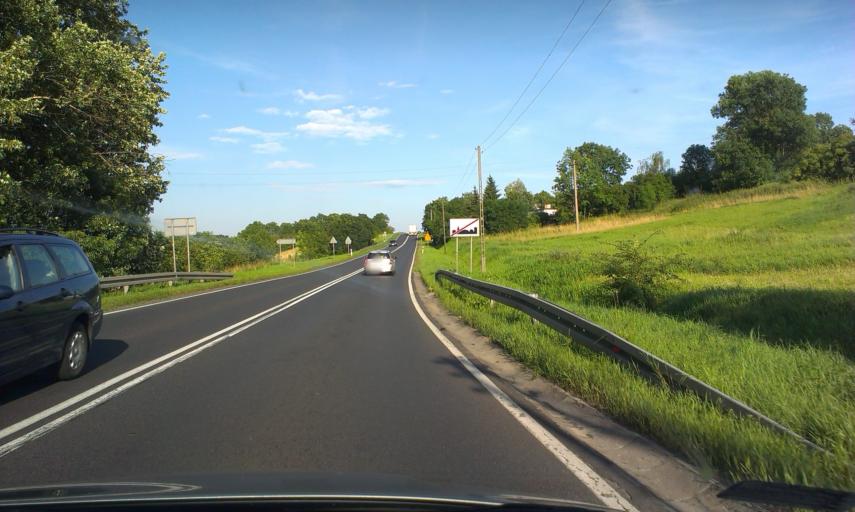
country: PL
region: Kujawsko-Pomorskie
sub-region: Powiat bydgoski
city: Sicienko
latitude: 53.1670
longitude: 17.7767
